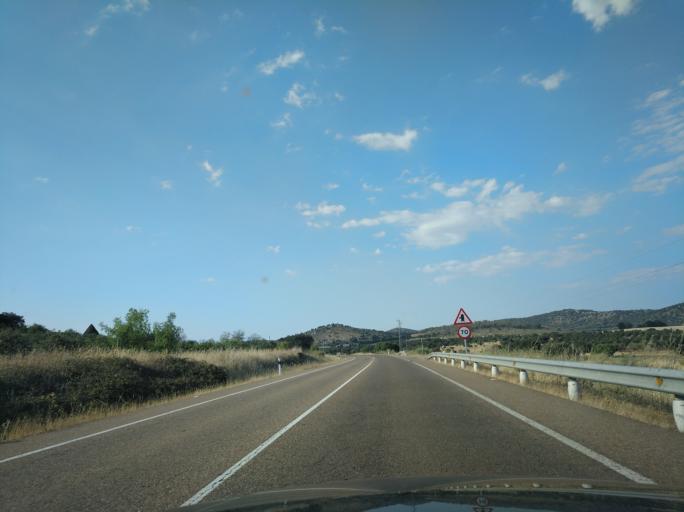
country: ES
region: Extremadura
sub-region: Provincia de Badajoz
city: Alconchel
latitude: 38.5213
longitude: -7.0649
